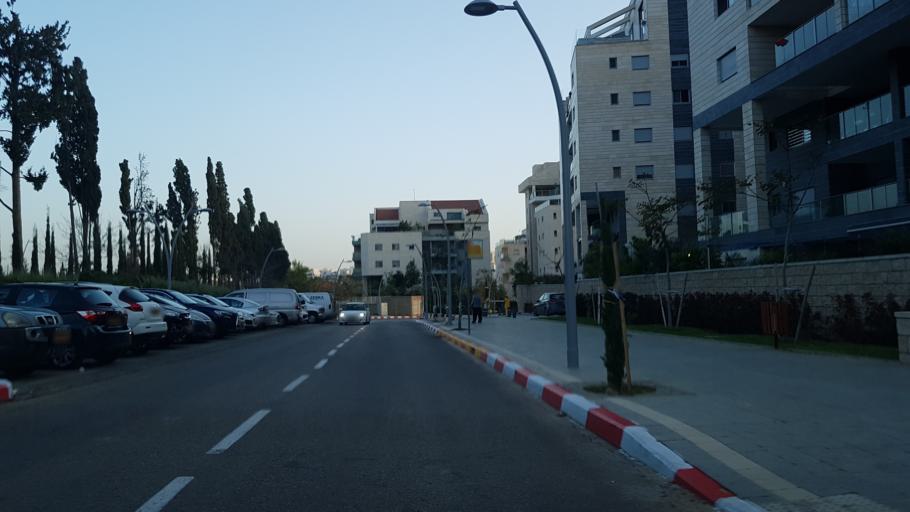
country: IL
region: Central District
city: Kfar Saba
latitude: 32.1960
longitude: 34.8971
